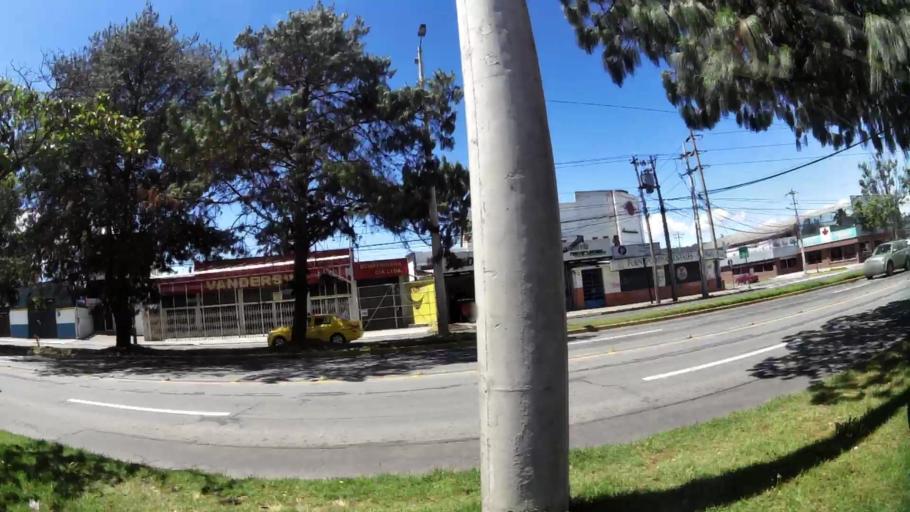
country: EC
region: Pichincha
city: Quito
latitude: -0.1612
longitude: -78.4858
